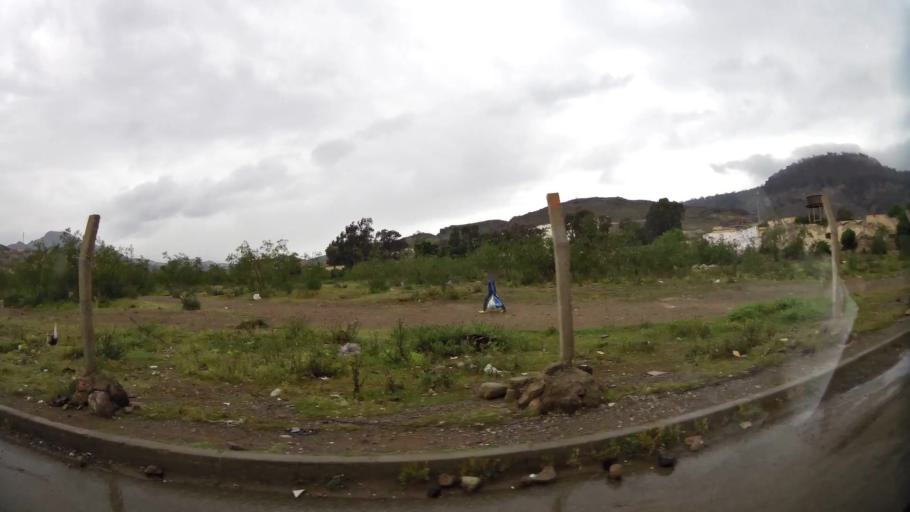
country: MA
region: Oriental
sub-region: Nador
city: Nador
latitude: 35.1493
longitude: -3.0049
